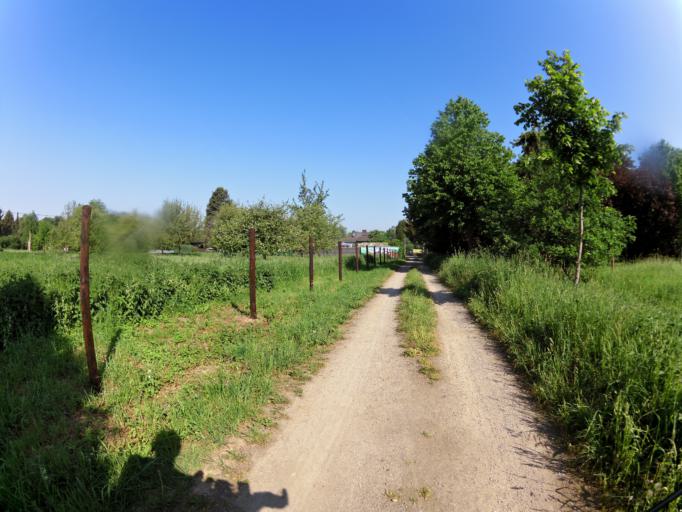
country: DE
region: North Rhine-Westphalia
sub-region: Regierungsbezirk Koln
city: Linnich
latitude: 50.9575
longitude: 6.3175
